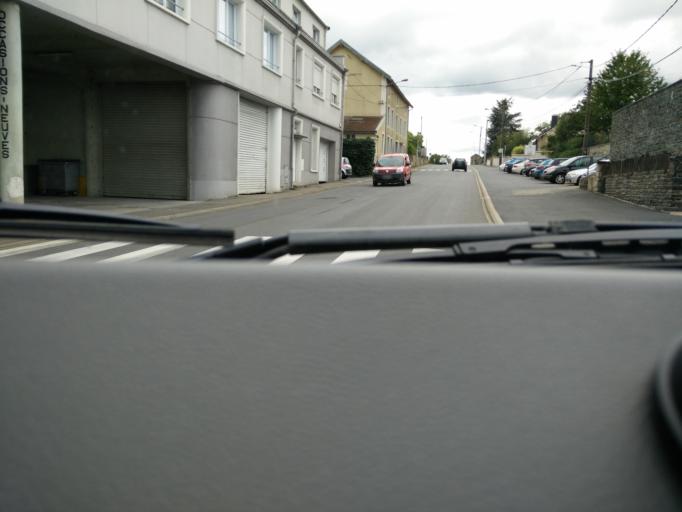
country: FR
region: Lorraine
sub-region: Departement de la Meuse
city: Stenay
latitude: 49.4926
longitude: 5.1925
